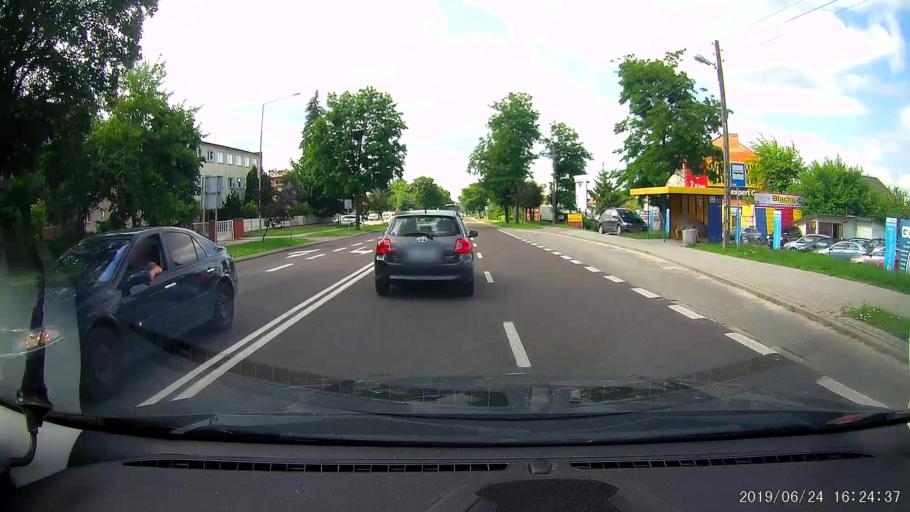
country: PL
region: Lublin Voivodeship
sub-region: Powiat tomaszowski
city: Tomaszow Lubelski
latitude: 50.4369
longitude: 23.4198
